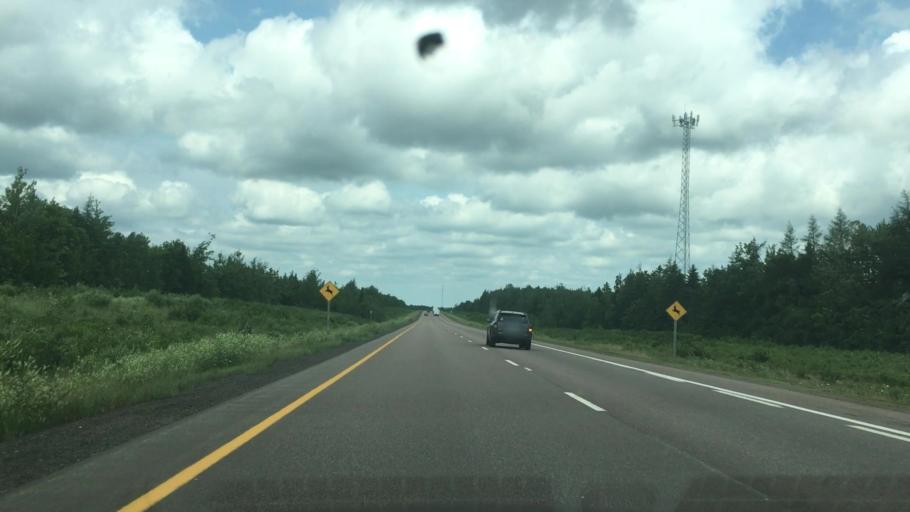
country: CA
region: New Brunswick
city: Dieppe
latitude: 46.0560
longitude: -64.5866
